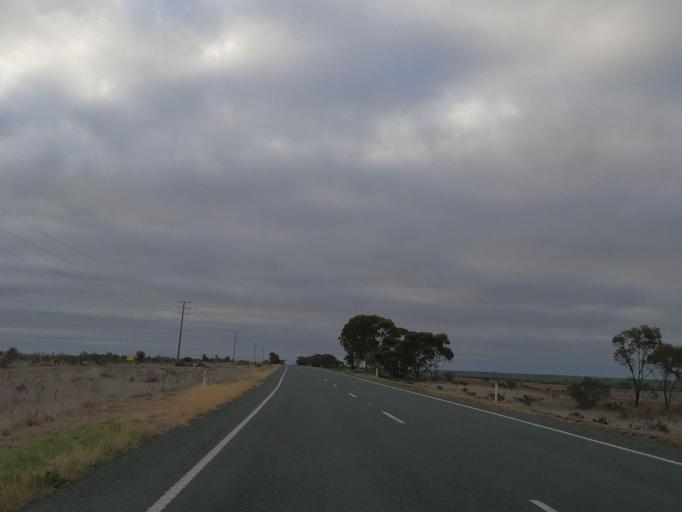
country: AU
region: Victoria
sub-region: Swan Hill
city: Swan Hill
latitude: -35.5751
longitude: 143.7876
